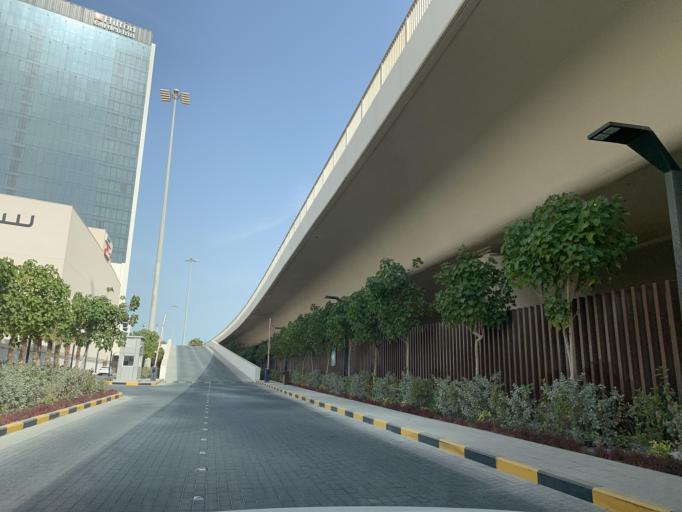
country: BH
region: Muharraq
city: Al Muharraq
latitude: 26.2485
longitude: 50.5871
